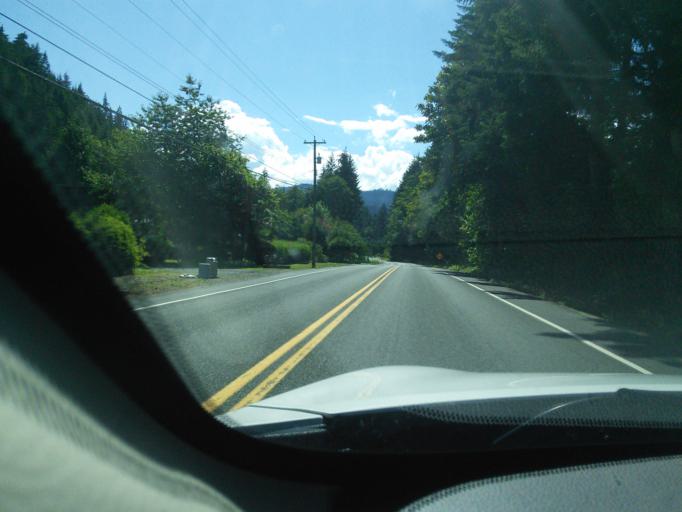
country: CA
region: British Columbia
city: Campbell River
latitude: 50.3350
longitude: -125.9152
